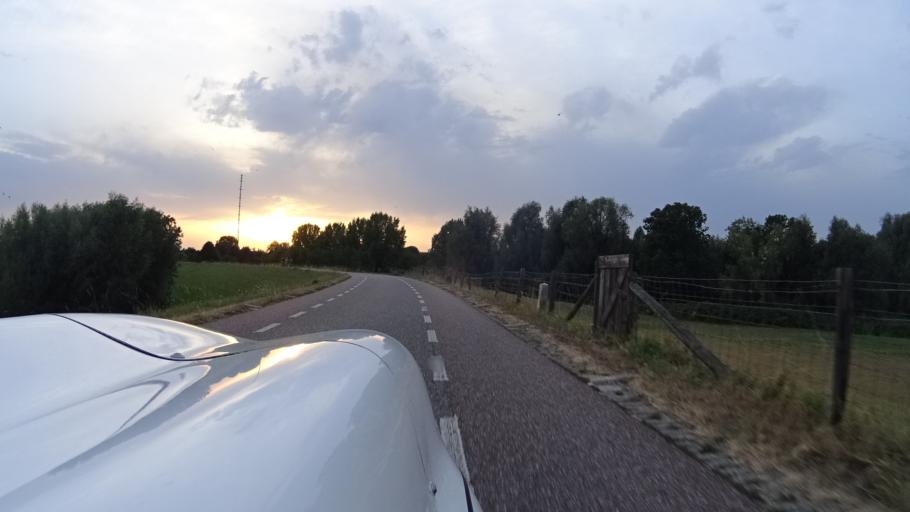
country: NL
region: Utrecht
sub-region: Gemeente Lopik
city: Lopik
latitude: 51.9667
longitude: 4.9453
